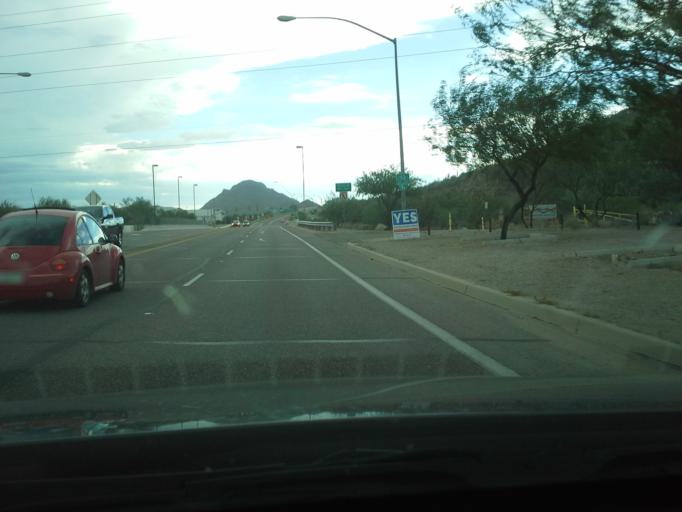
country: US
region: Arizona
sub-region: Pima County
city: South Tucson
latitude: 32.2067
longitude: -110.9876
